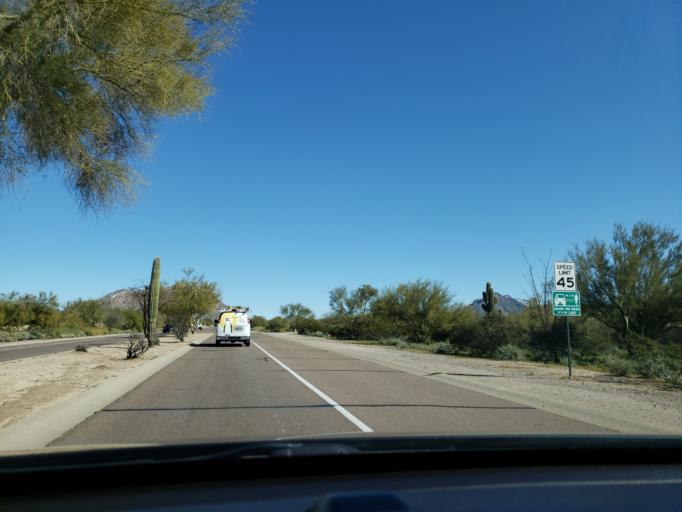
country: US
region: Arizona
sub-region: Maricopa County
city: Carefree
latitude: 33.7126
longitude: -111.8816
